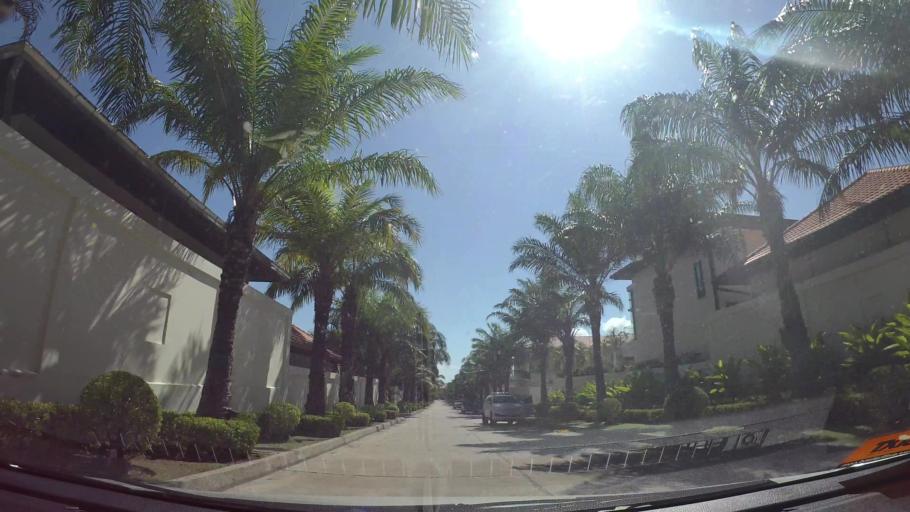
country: TH
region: Chon Buri
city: Phatthaya
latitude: 12.9167
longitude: 100.8599
